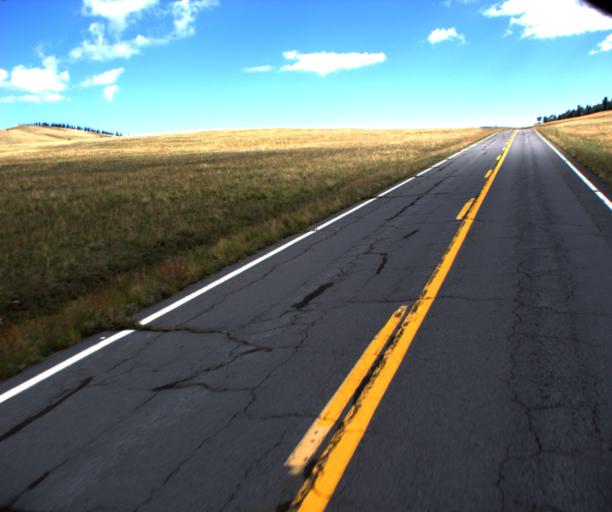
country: US
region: Arizona
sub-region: Apache County
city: Eagar
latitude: 33.9742
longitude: -109.3778
